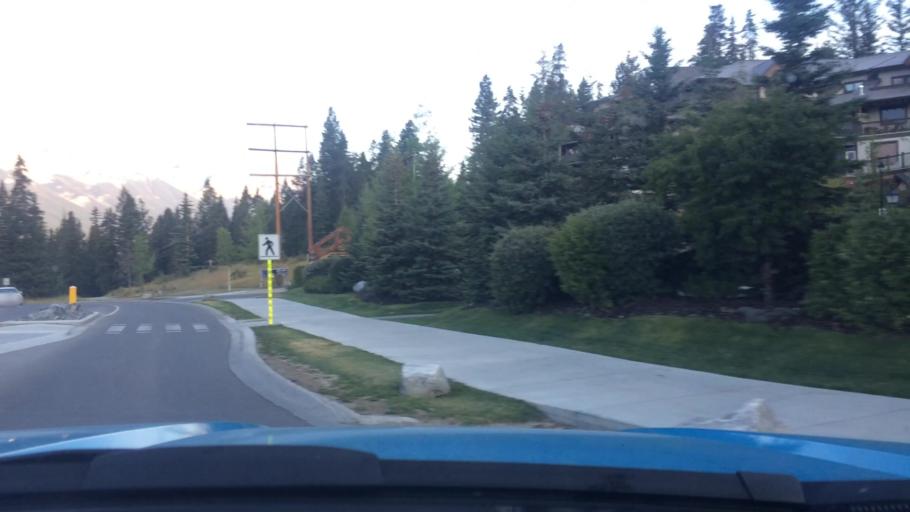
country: CA
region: Alberta
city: Canmore
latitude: 51.0866
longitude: -115.3280
